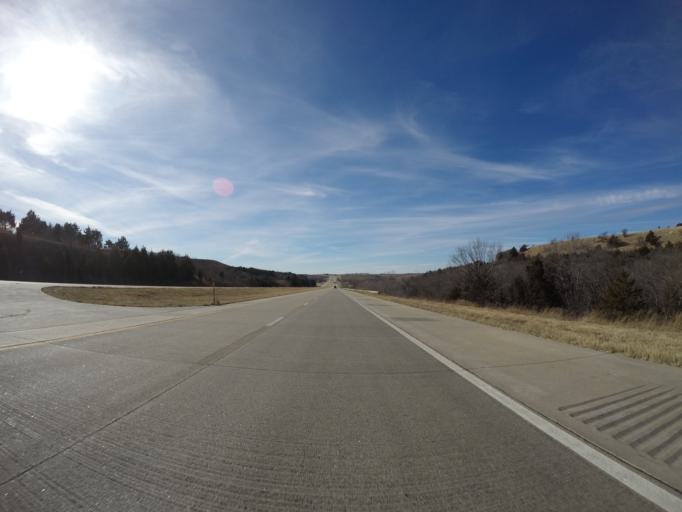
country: US
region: Kansas
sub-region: Riley County
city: Ogden
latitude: 39.0630
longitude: -96.7122
